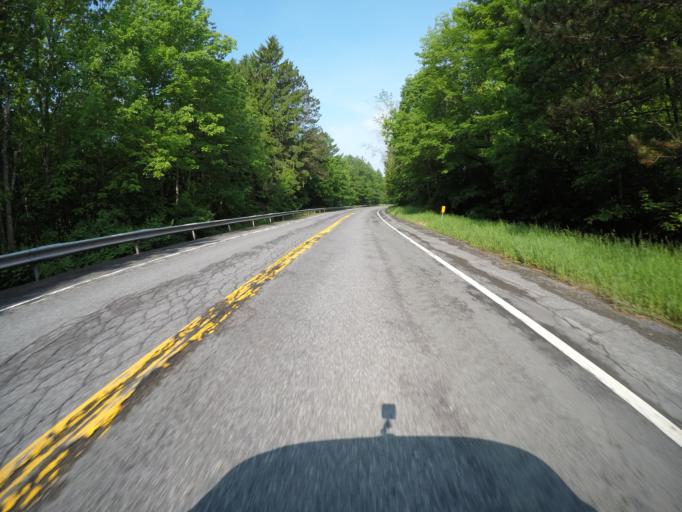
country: US
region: New York
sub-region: Sullivan County
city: Livingston Manor
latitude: 42.1201
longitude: -74.7311
